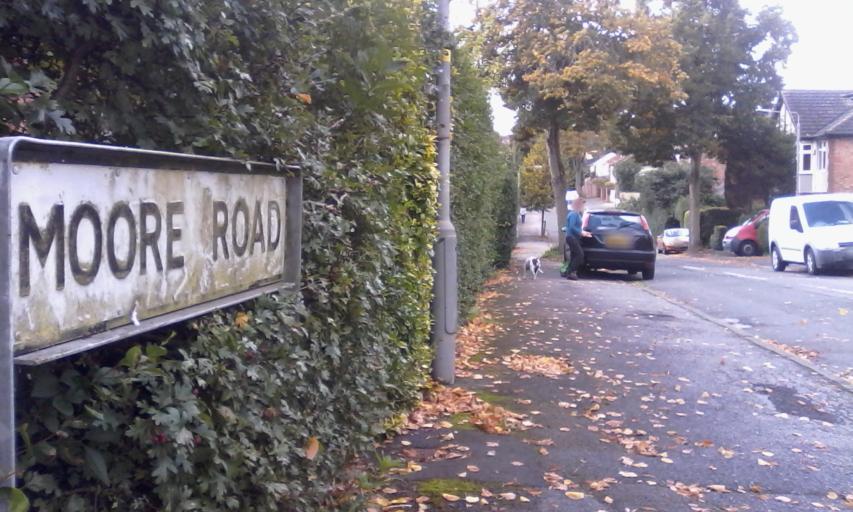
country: GB
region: England
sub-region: Nottinghamshire
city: Arnold
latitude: 52.9805
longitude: -1.1181
